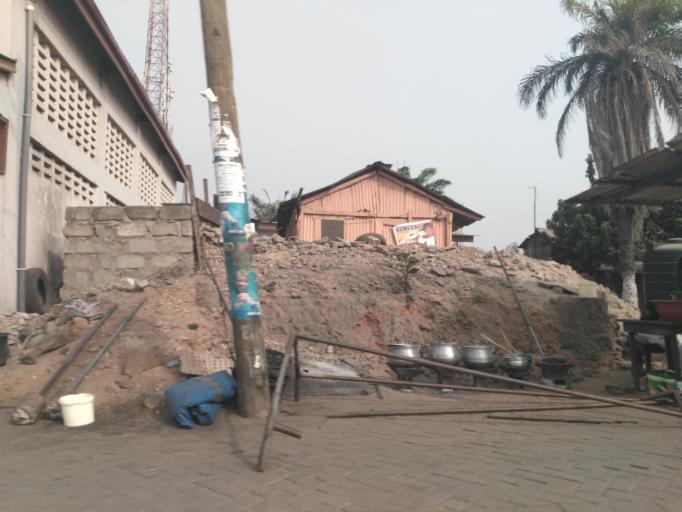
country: GH
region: Greater Accra
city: Accra
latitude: 5.5405
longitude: -0.2165
